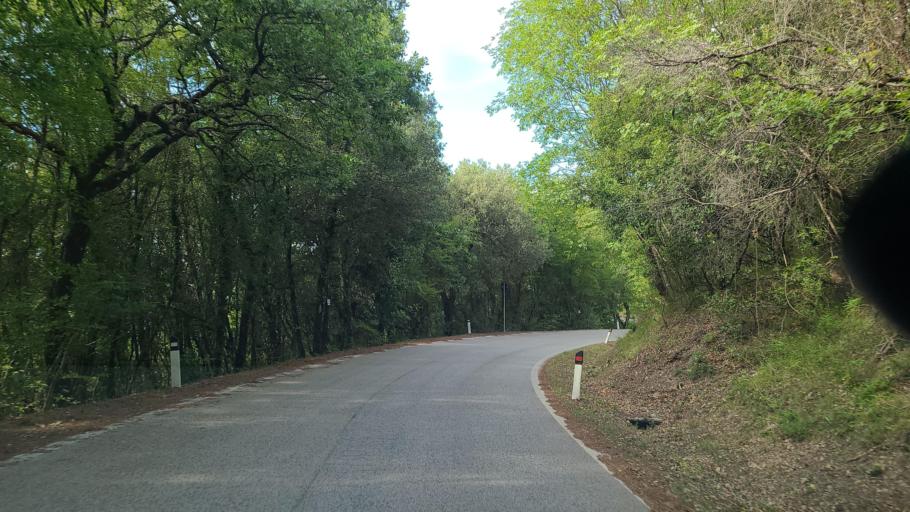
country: IT
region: Tuscany
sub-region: Provincia di Siena
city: San Gimignano
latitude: 43.4181
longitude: 10.9761
